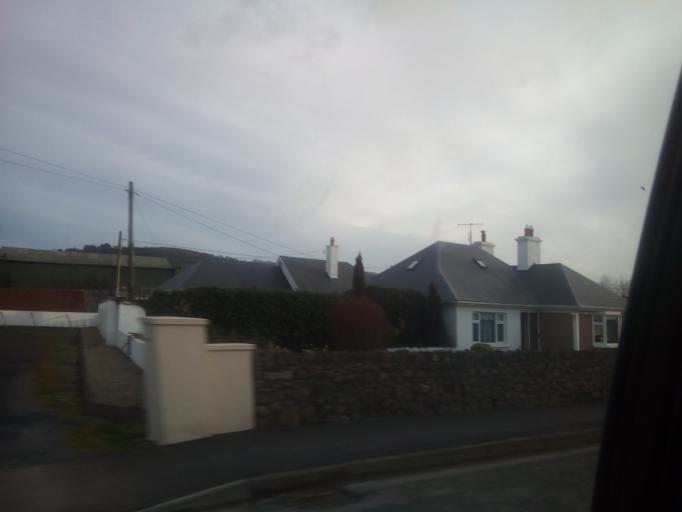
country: IE
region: Leinster
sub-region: Laois
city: Abbeyleix
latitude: 52.8419
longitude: -7.4016
